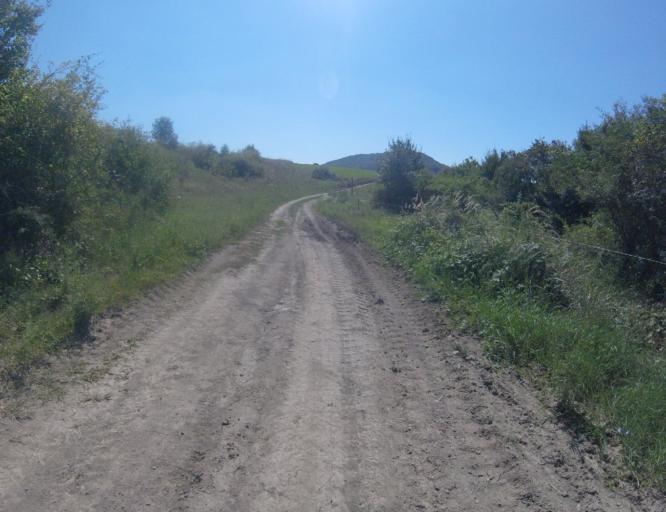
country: HU
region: Nograd
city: Rimoc
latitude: 47.9927
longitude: 19.5874
